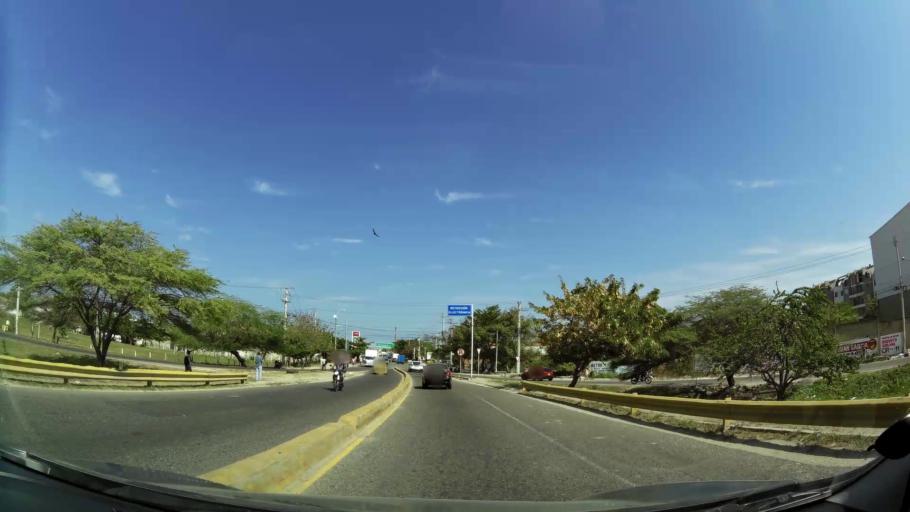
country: CO
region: Atlantico
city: Barranquilla
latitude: 10.9432
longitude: -74.8318
